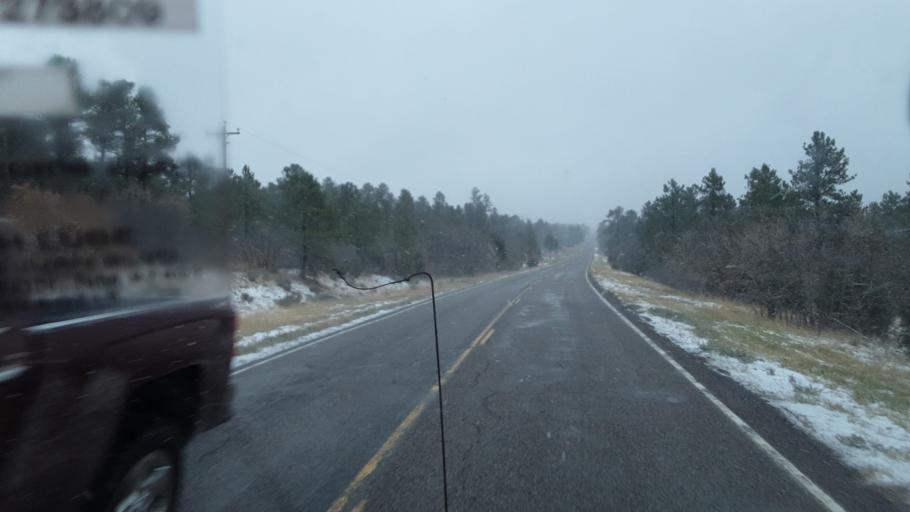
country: US
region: New Mexico
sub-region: Rio Arriba County
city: Tierra Amarilla
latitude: 36.6696
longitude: -106.5572
